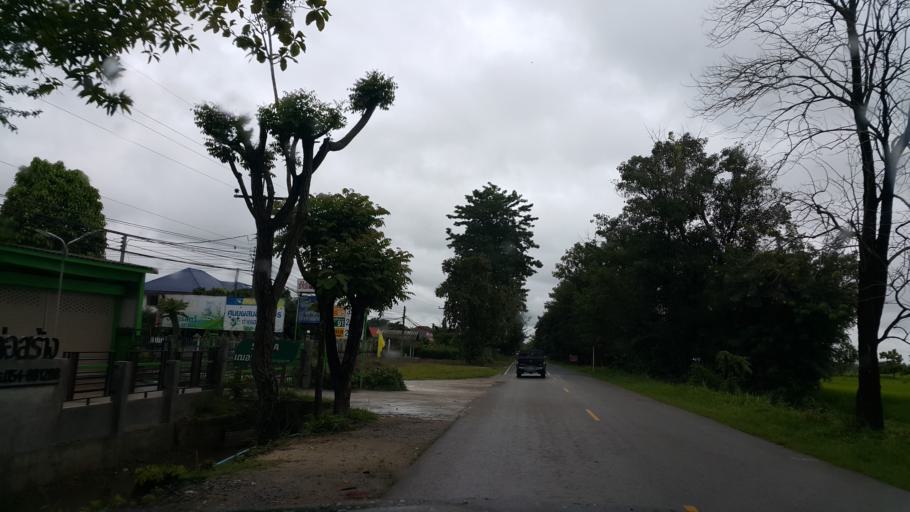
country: TH
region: Phayao
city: Chiang Kham
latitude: 19.5232
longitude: 100.3541
